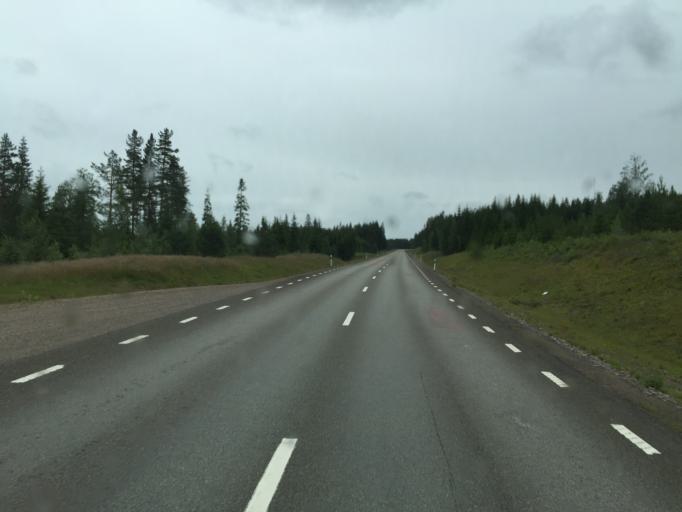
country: SE
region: Dalarna
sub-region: Malung-Saelens kommun
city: Malung
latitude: 60.5932
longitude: 13.5802
